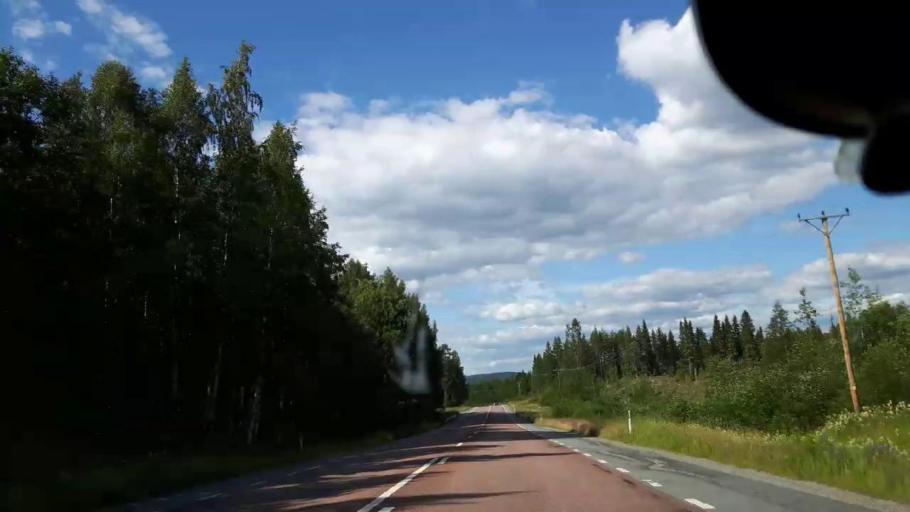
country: SE
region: Jaemtland
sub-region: Braecke Kommun
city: Braecke
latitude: 62.8043
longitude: 15.3700
